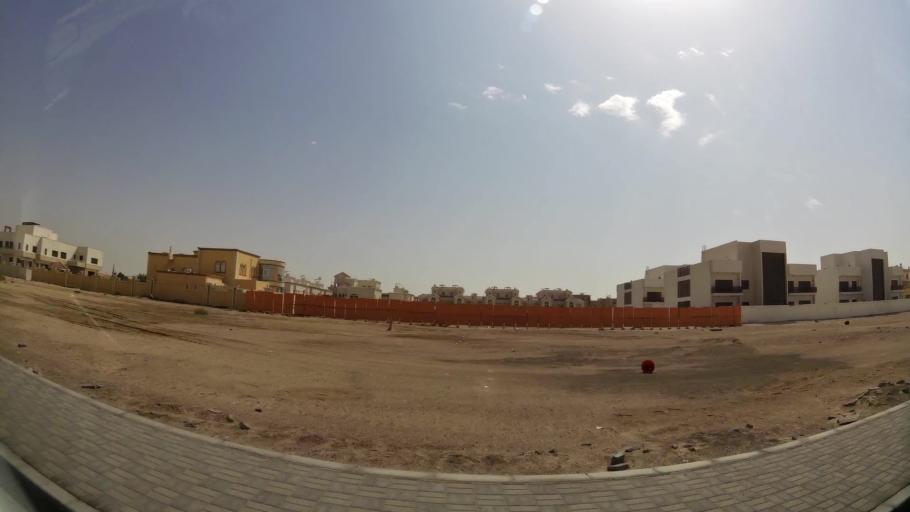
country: AE
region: Abu Dhabi
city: Abu Dhabi
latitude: 24.3474
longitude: 54.5455
